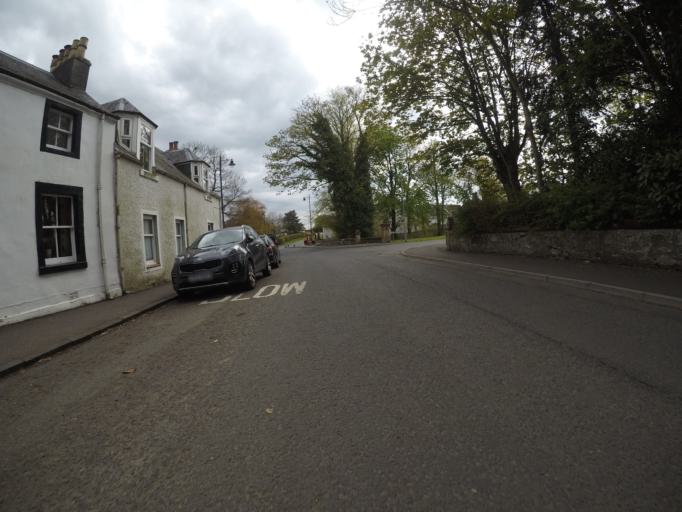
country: GB
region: Scotland
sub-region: East Ayrshire
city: Kilmarnock
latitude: 55.6538
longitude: -4.4468
